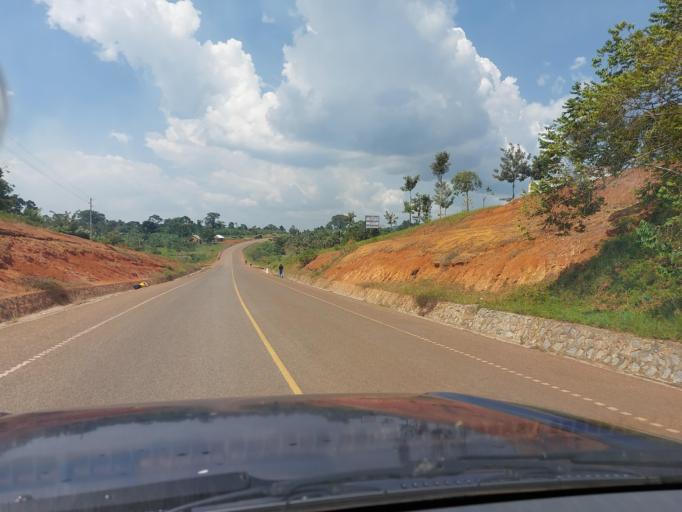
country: UG
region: Central Region
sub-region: Buikwe District
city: Buikwe
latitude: 0.3042
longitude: 33.0967
